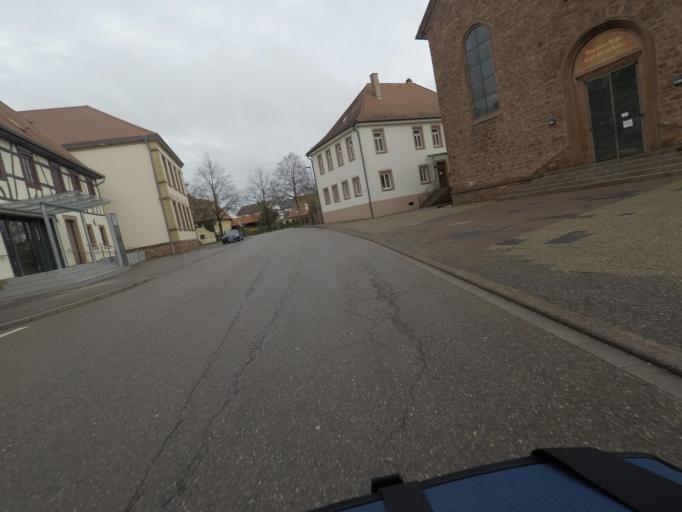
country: DE
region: Baden-Wuerttemberg
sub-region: Karlsruhe Region
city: Au am Rhein
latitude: 48.9512
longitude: 8.2390
